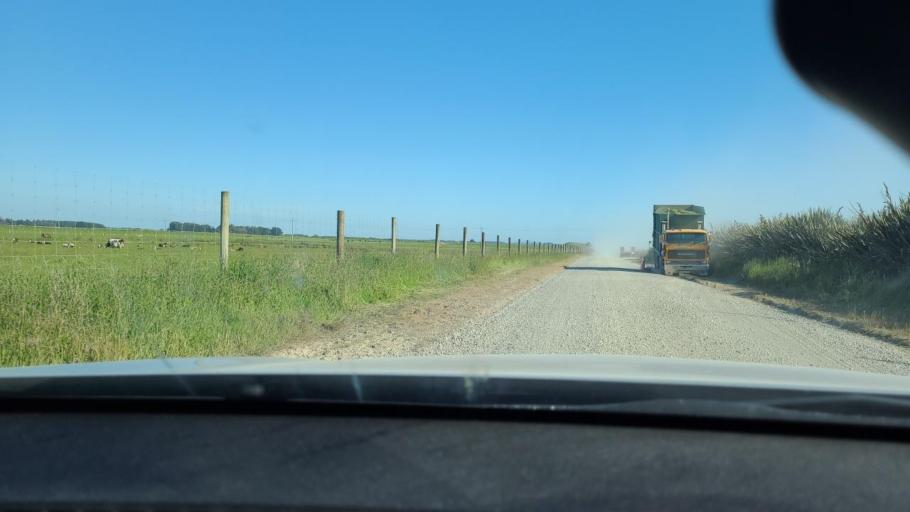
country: NZ
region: Southland
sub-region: Invercargill City
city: Invercargill
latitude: -46.3403
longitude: 168.2429
